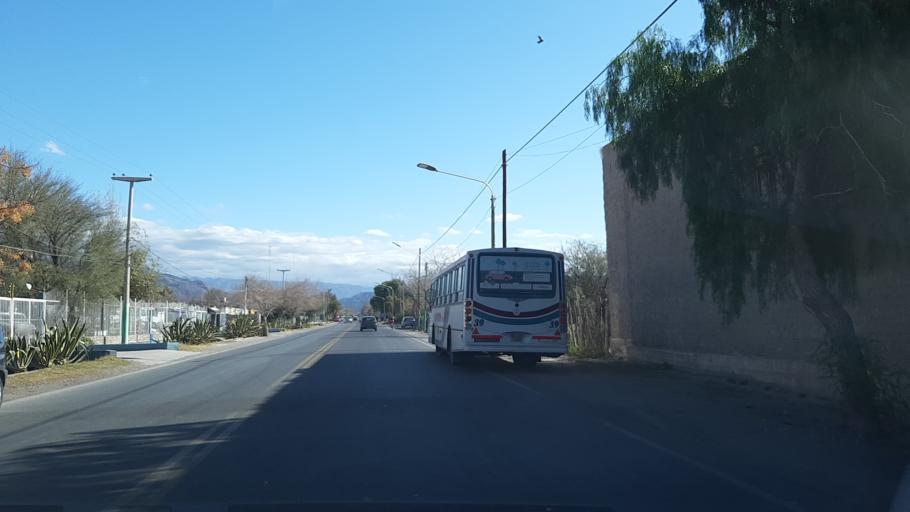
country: AR
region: San Juan
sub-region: Departamento de Rivadavia
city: Rivadavia
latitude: -31.5392
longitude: -68.6129
